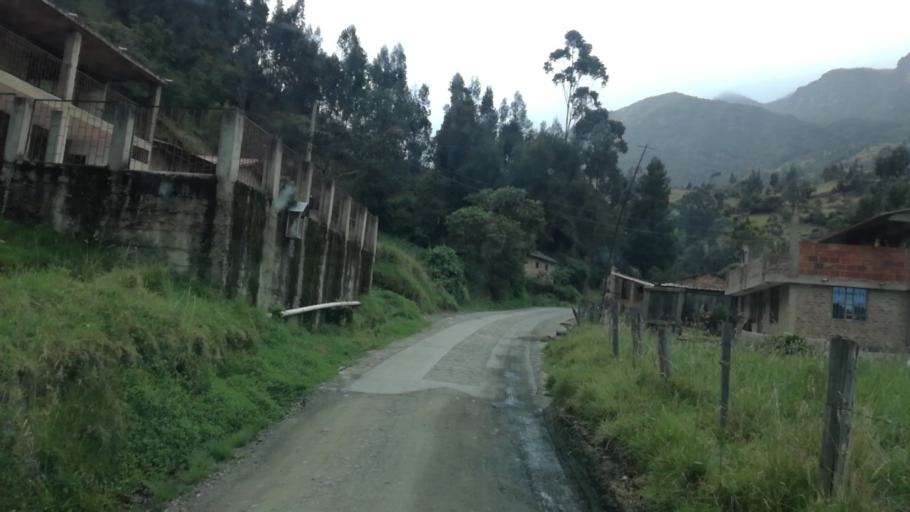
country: CO
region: Boyaca
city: Socha Viejo
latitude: 5.9411
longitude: -72.6885
